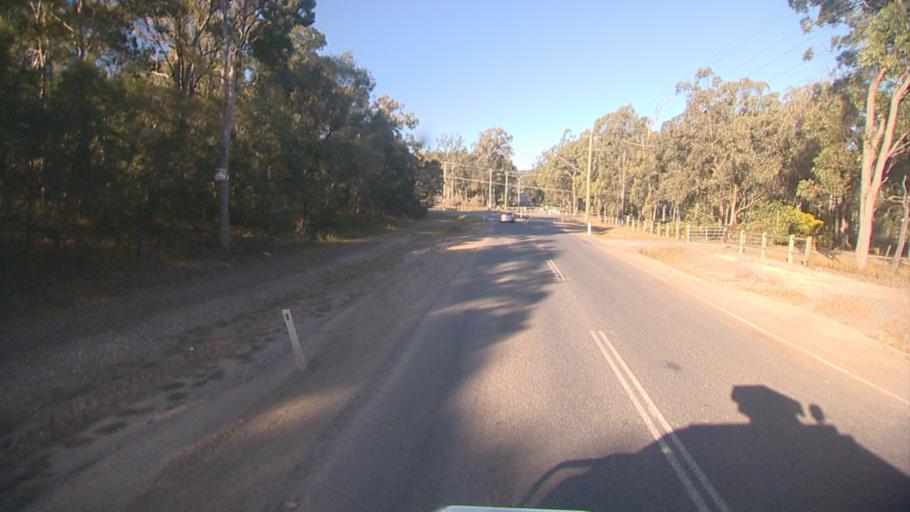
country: AU
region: Queensland
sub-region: Logan
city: Chambers Flat
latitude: -27.7702
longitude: 153.1364
